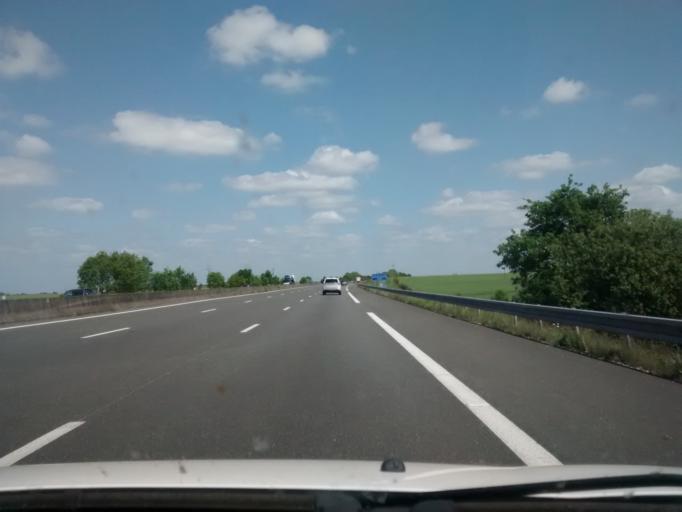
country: FR
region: Centre
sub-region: Departement d'Eure-et-Loir
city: Brou
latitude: 48.2751
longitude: 1.1760
